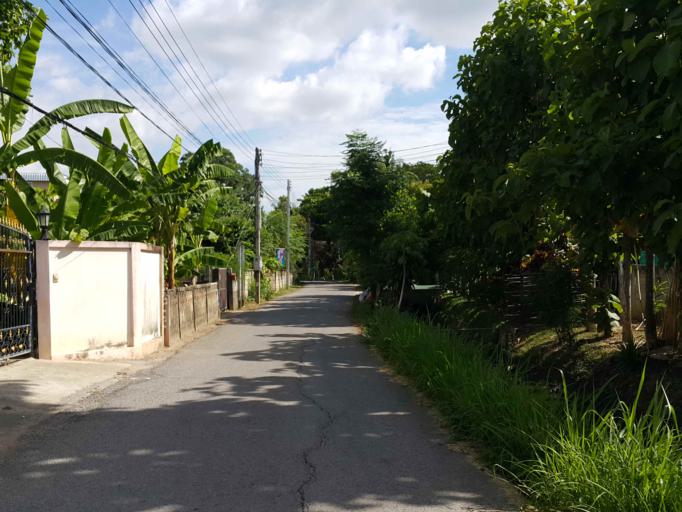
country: TH
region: Chiang Mai
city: Saraphi
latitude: 18.7408
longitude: 98.9979
